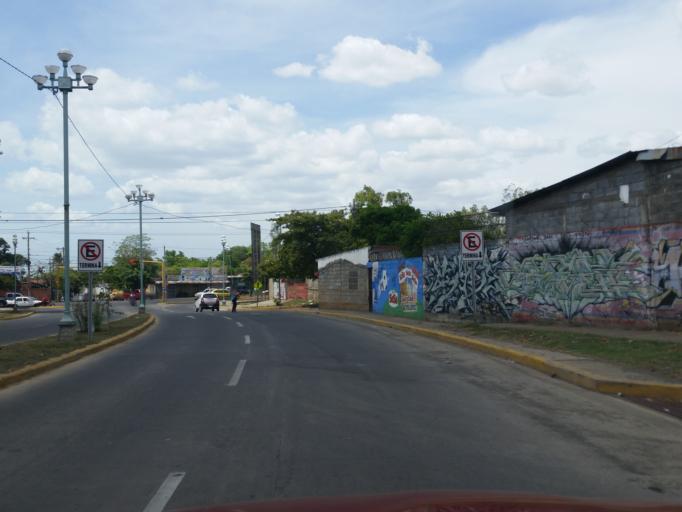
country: NI
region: Managua
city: Managua
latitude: 12.1287
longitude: -86.2462
